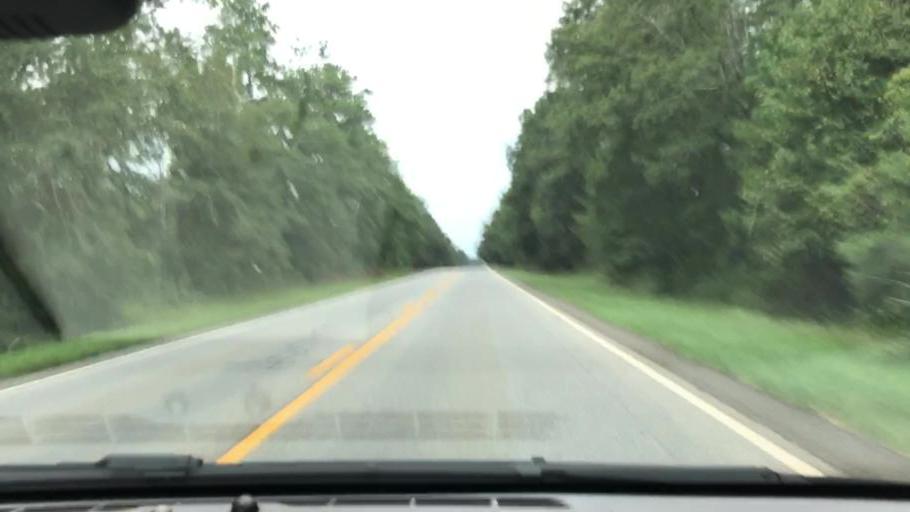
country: US
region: Georgia
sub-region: Early County
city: Blakely
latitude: 31.2927
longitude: -85.0615
